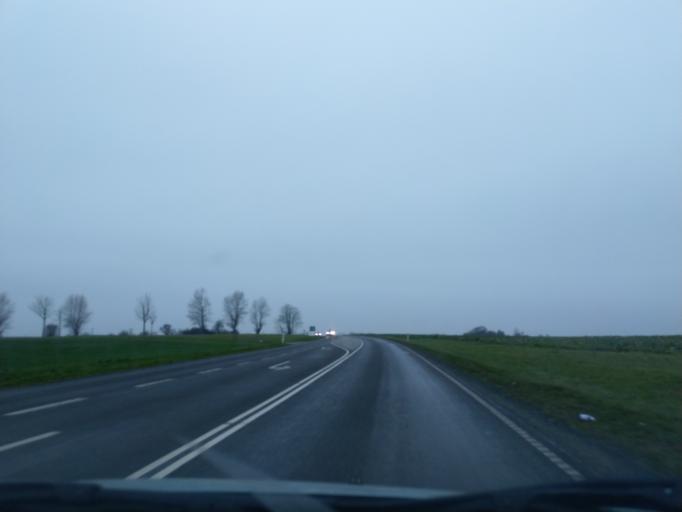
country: DK
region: Zealand
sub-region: Vordingborg Kommune
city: Praesto
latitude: 55.1185
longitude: 12.0218
